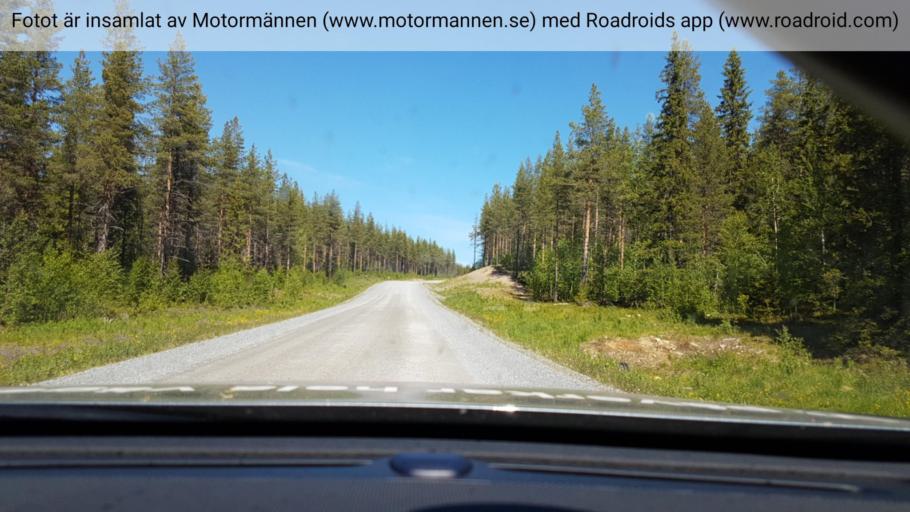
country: SE
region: Vaesterbotten
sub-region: Vilhelmina Kommun
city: Sjoberg
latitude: 64.6650
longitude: 15.7557
